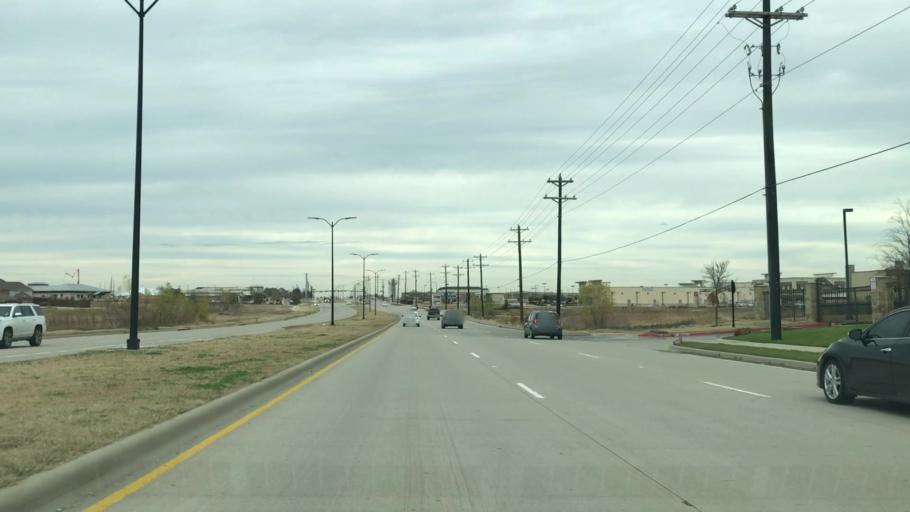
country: US
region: Texas
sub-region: Denton County
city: The Colony
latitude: 33.1216
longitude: -96.8915
